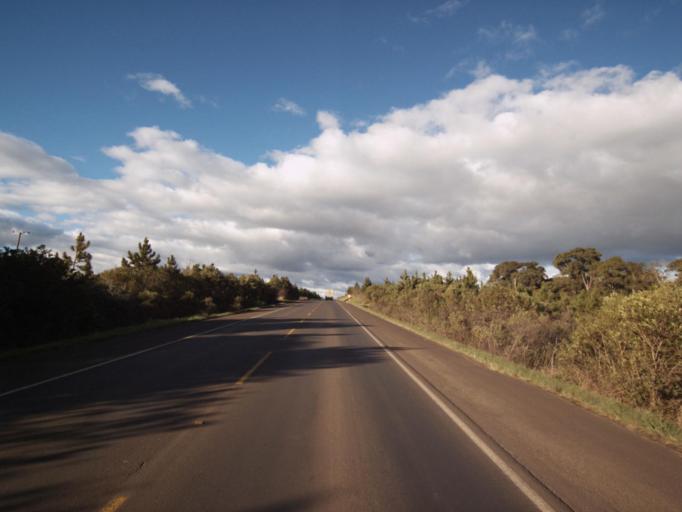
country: BR
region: Santa Catarina
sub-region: Campos Novos
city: Campos Novos
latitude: -27.3593
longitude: -51.2943
